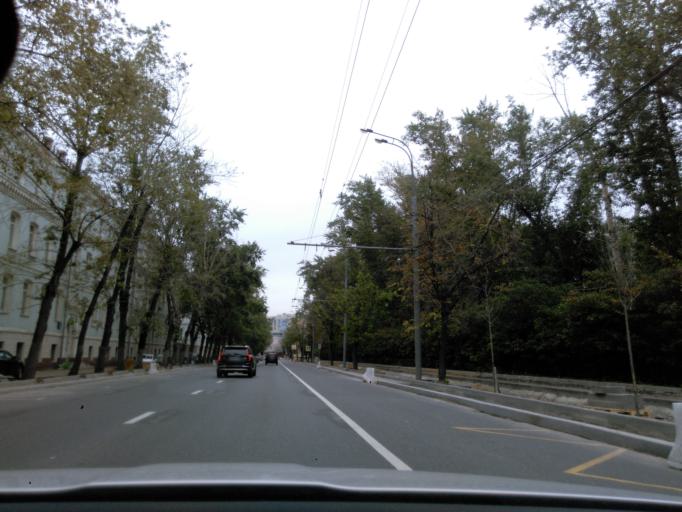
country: RU
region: Moscow
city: Zamoskvorech'ye
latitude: 55.7155
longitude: 37.6256
